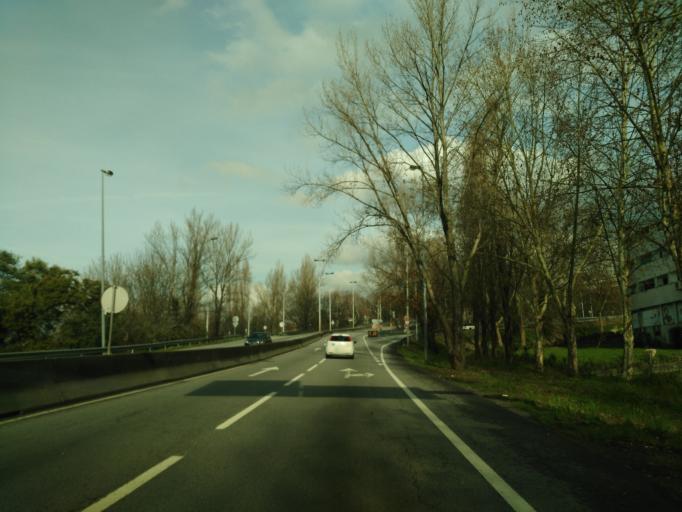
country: PT
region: Braga
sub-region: Guimaraes
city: Guimaraes
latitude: 41.4486
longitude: -8.3072
